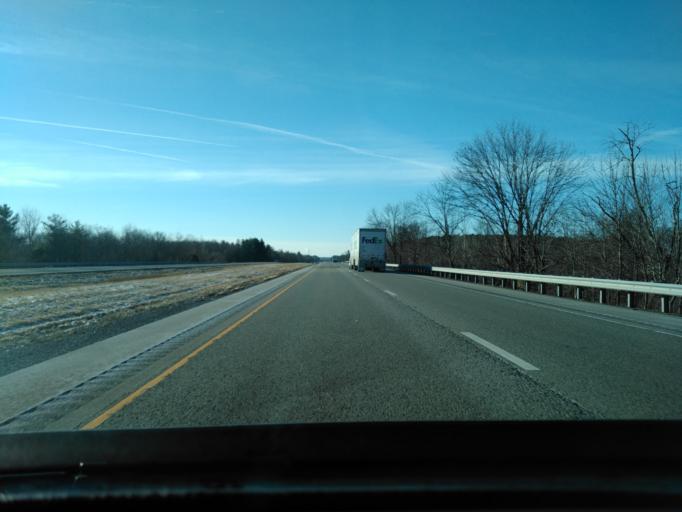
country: US
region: Illinois
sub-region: Williamson County
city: Johnston City
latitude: 37.8548
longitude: -88.9433
